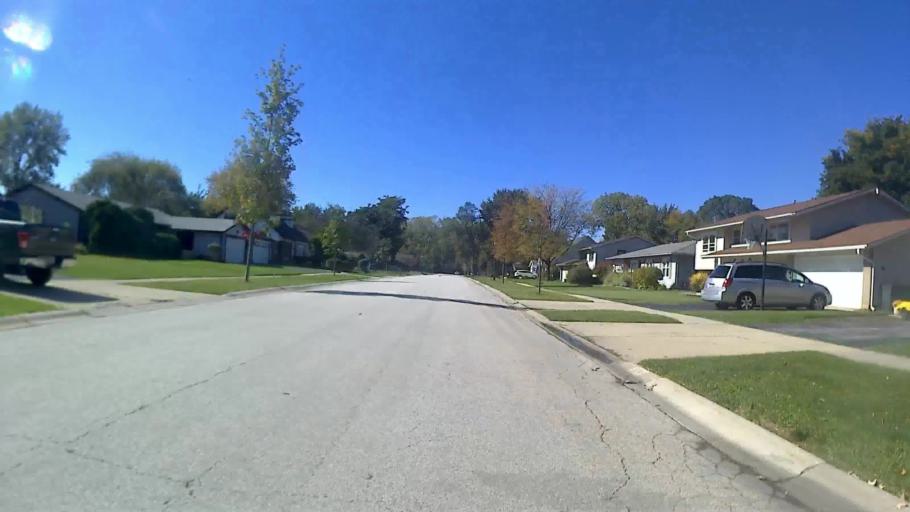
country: US
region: Illinois
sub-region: DuPage County
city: Itasca
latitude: 42.0013
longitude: -88.0149
